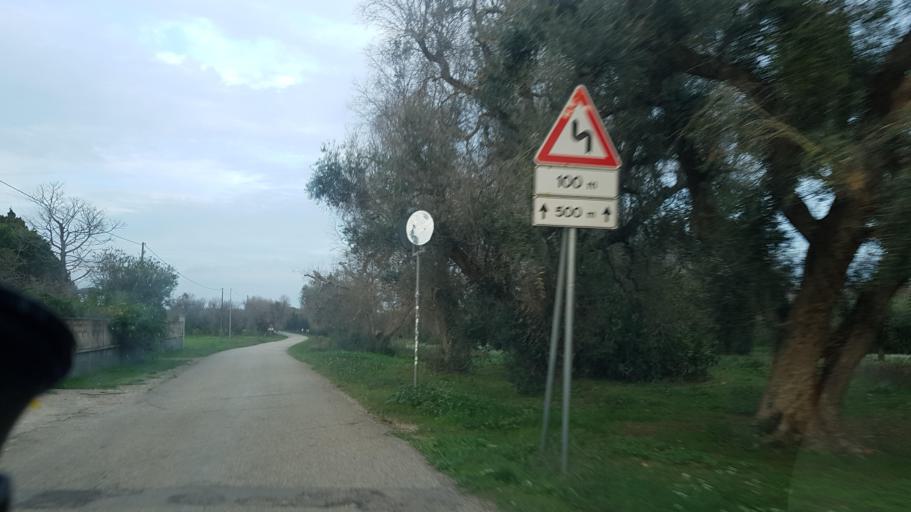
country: IT
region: Apulia
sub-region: Provincia di Brindisi
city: Mesagne
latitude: 40.5394
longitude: 17.7796
